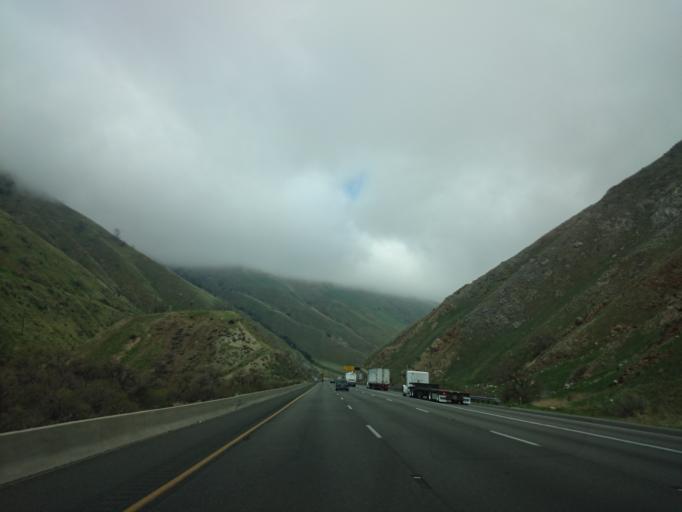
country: US
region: California
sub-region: Kern County
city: Lebec
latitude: 34.8915
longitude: -118.9135
